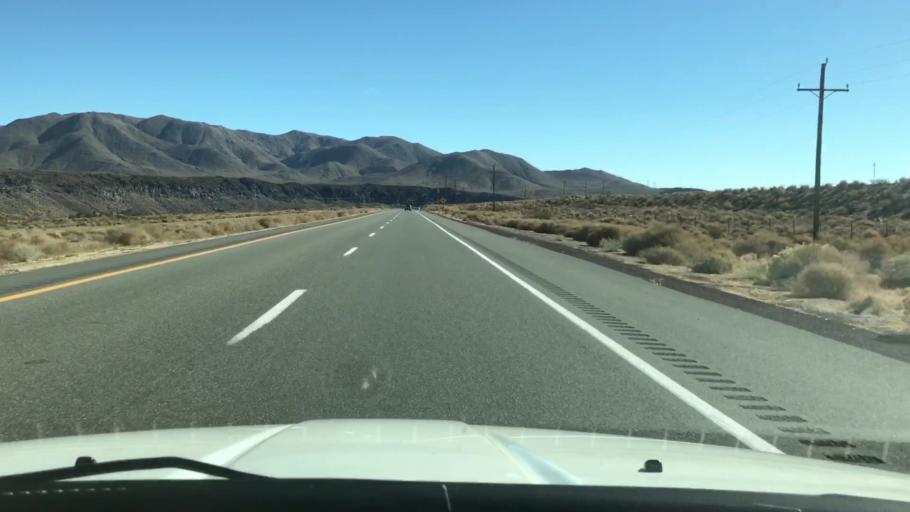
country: US
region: California
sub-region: Kern County
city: Inyokern
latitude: 35.9613
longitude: -117.9150
